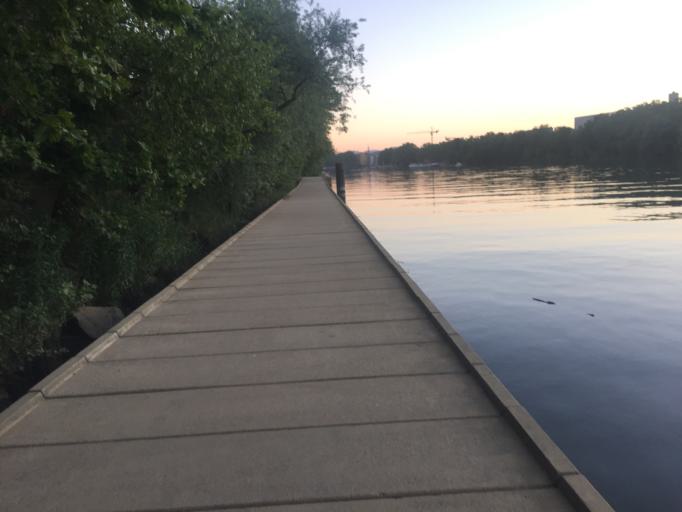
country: FR
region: Rhone-Alpes
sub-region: Departement du Rhone
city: Caluire-et-Cuire
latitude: 45.7901
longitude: 4.8207
